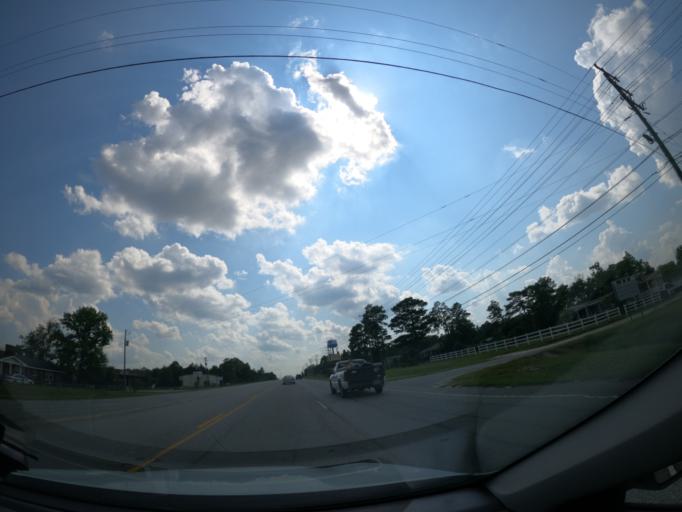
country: US
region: South Carolina
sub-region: Lexington County
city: South Congaree
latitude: 33.8932
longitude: -81.1583
